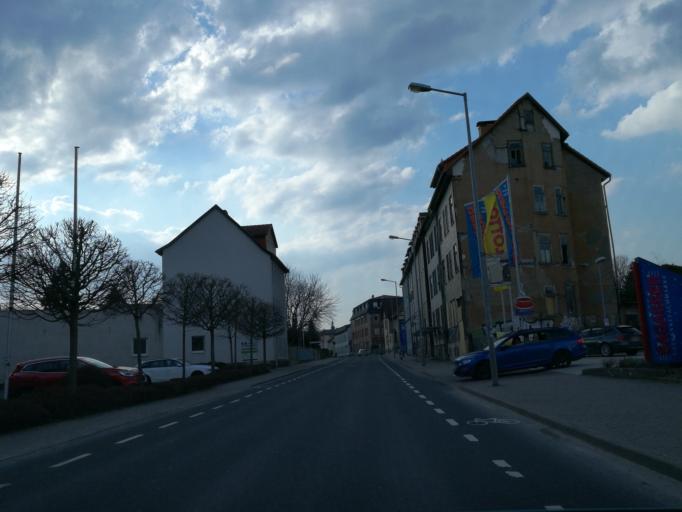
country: DE
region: Thuringia
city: Neuhaus
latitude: 50.6821
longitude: 10.9260
